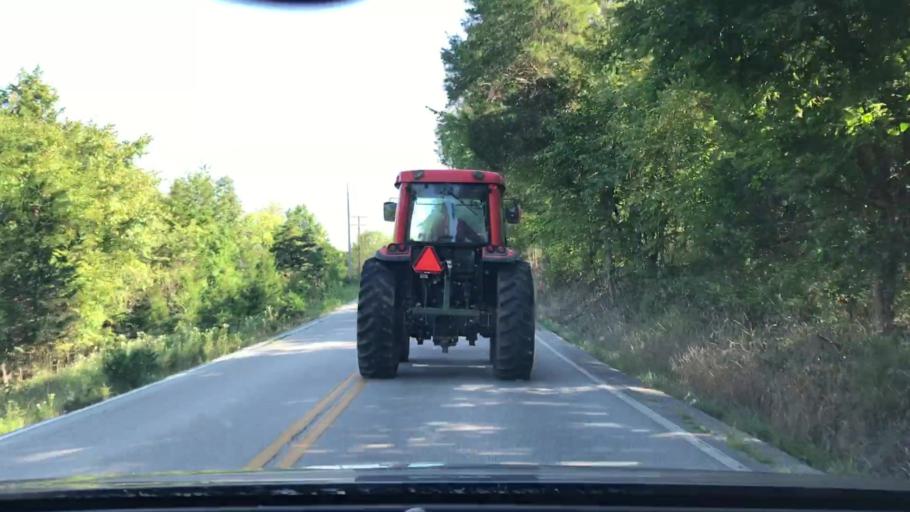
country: US
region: Tennessee
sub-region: Smith County
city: Carthage
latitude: 36.3007
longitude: -85.9530
